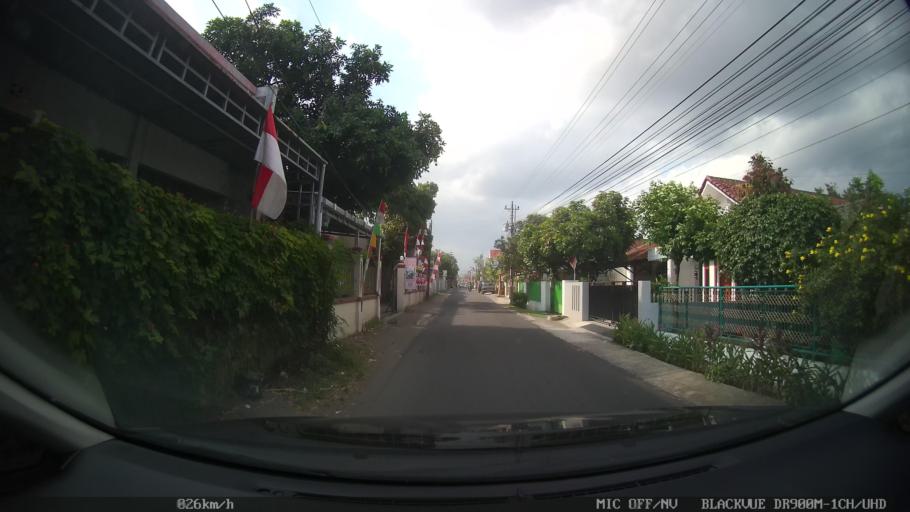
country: ID
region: Daerah Istimewa Yogyakarta
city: Gamping Lor
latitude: -7.8001
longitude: 110.3448
